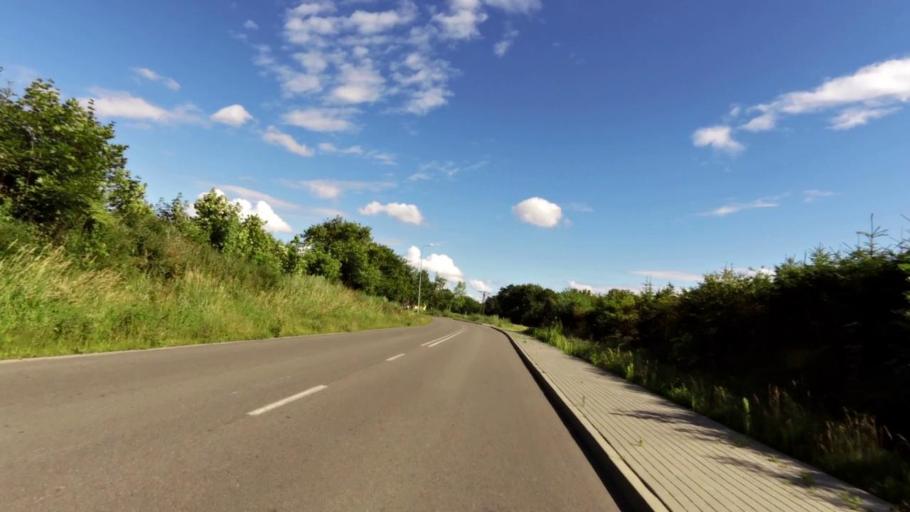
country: PL
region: West Pomeranian Voivodeship
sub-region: Powiat slawienski
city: Slawno
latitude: 54.4560
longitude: 16.7391
